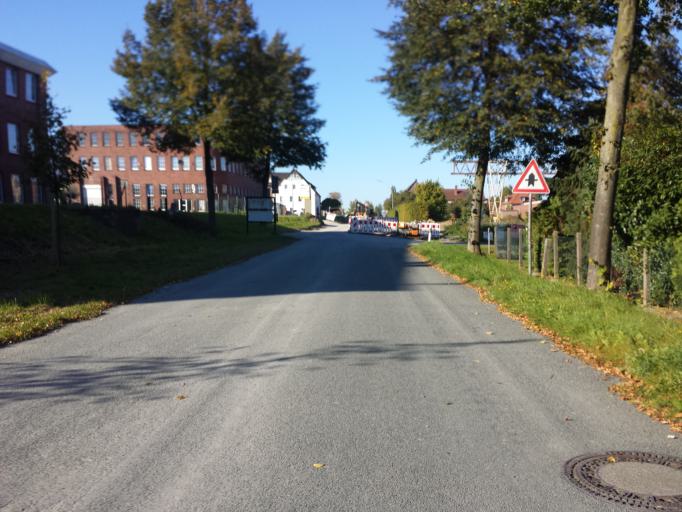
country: DE
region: North Rhine-Westphalia
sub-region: Regierungsbezirk Detmold
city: Langenberg
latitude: 51.7741
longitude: 8.3233
